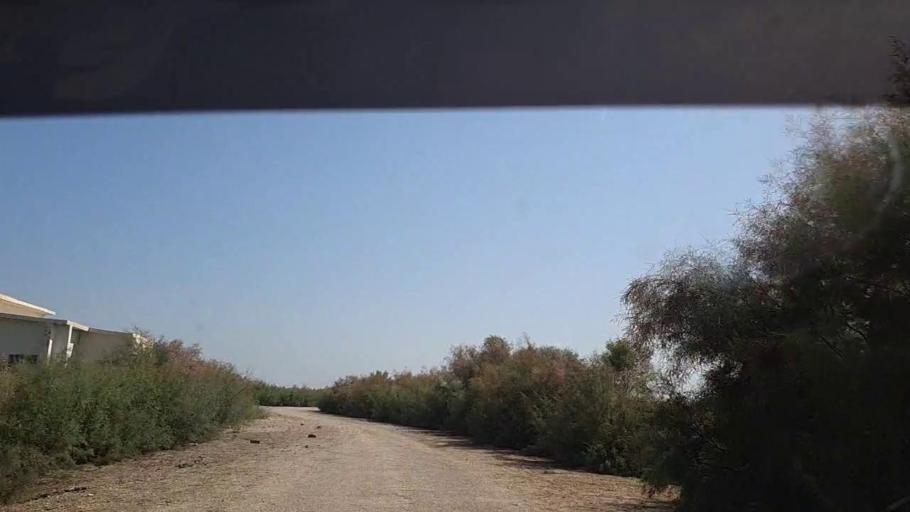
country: PK
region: Sindh
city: Ghauspur
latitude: 28.2049
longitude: 69.0765
